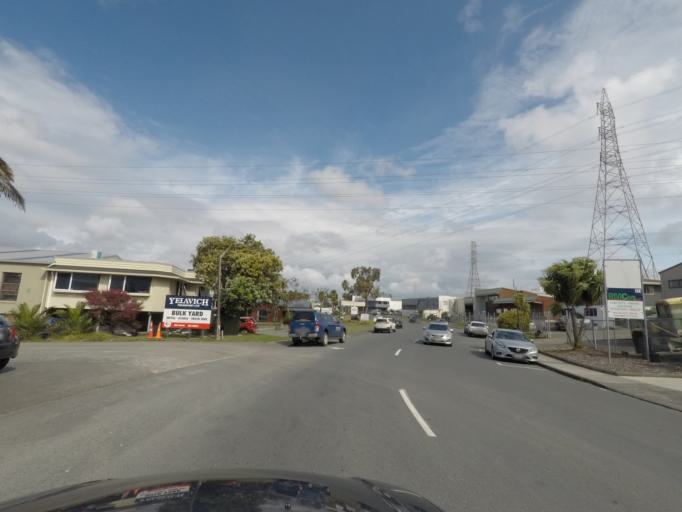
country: NZ
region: Auckland
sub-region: Auckland
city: Rosebank
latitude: -36.8473
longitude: 174.6334
